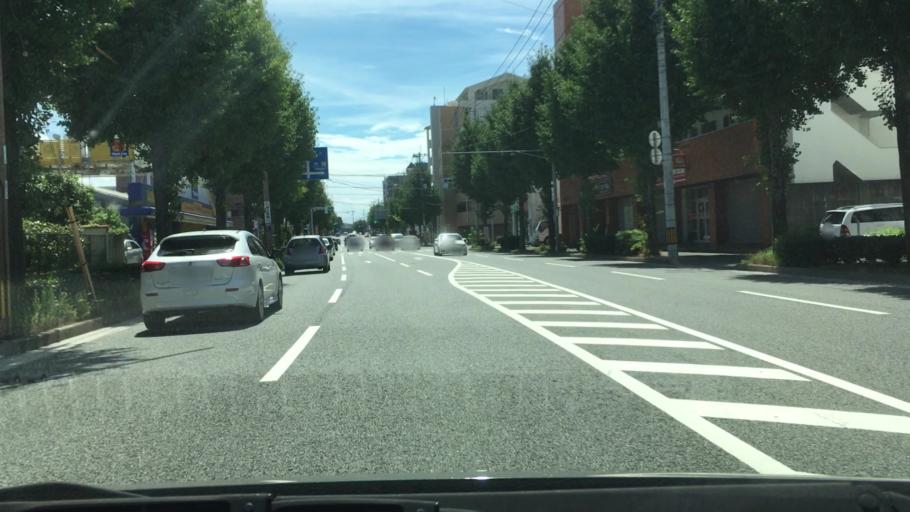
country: JP
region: Fukuoka
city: Fukuoka-shi
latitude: 33.5647
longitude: 130.4295
